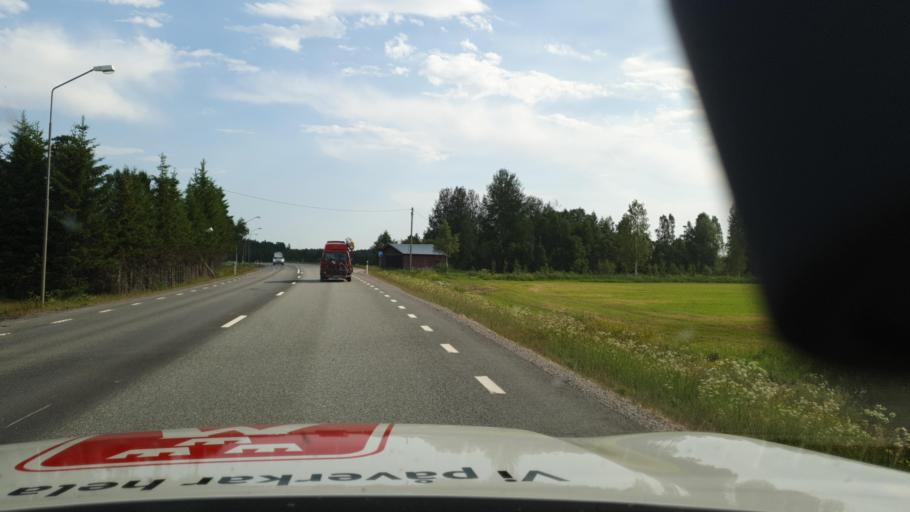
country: SE
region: Vaesterbotten
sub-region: Skelleftea Kommun
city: Burea
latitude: 64.5103
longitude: 21.2568
